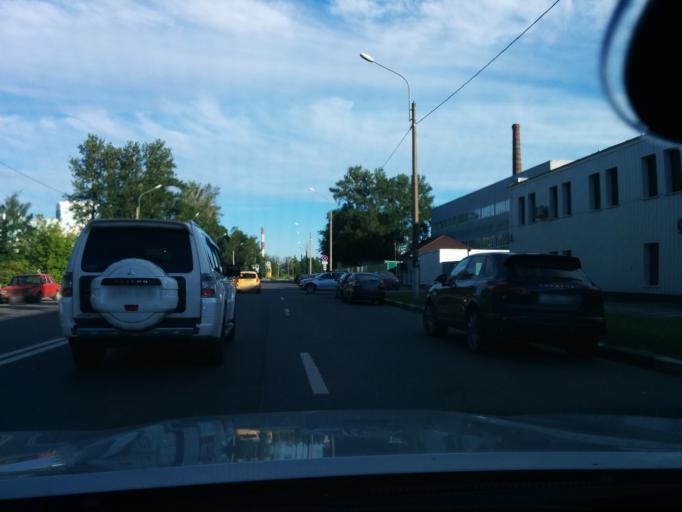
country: RU
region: St.-Petersburg
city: Kushelevka
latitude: 59.9822
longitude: 30.3643
